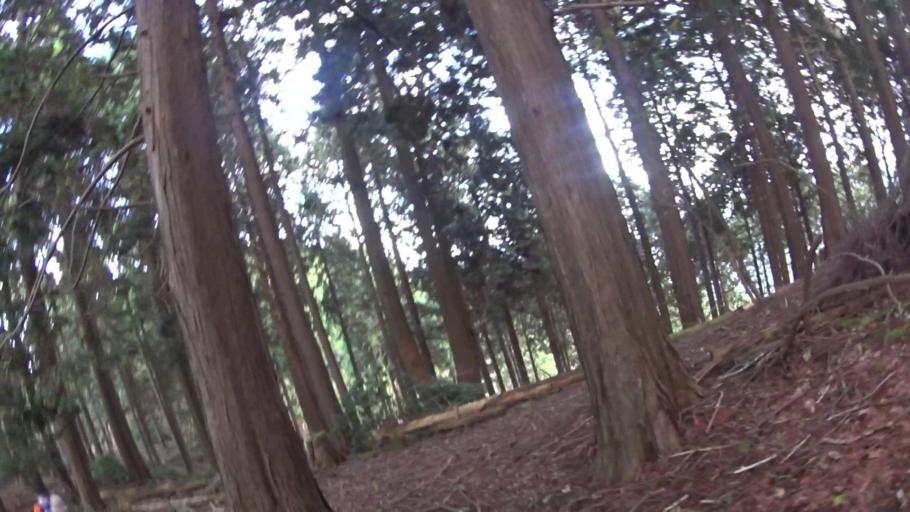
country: JP
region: Shiga Prefecture
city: Otsu-shi
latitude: 35.0996
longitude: 135.8393
